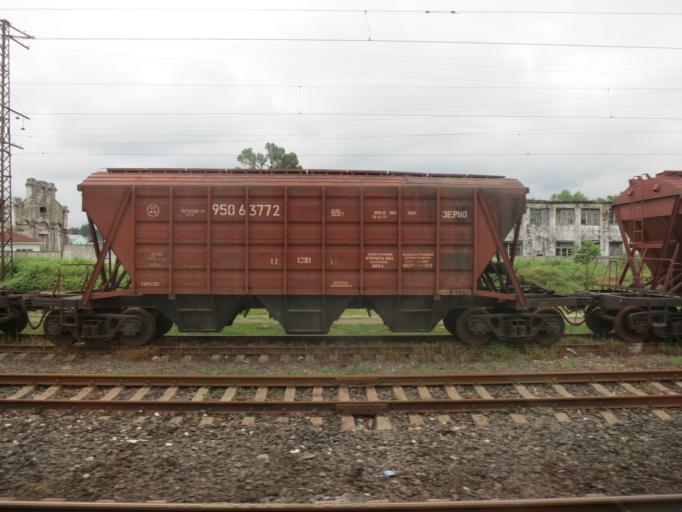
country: GE
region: Ajaria
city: Kobuleti
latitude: 41.8085
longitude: 41.7798
